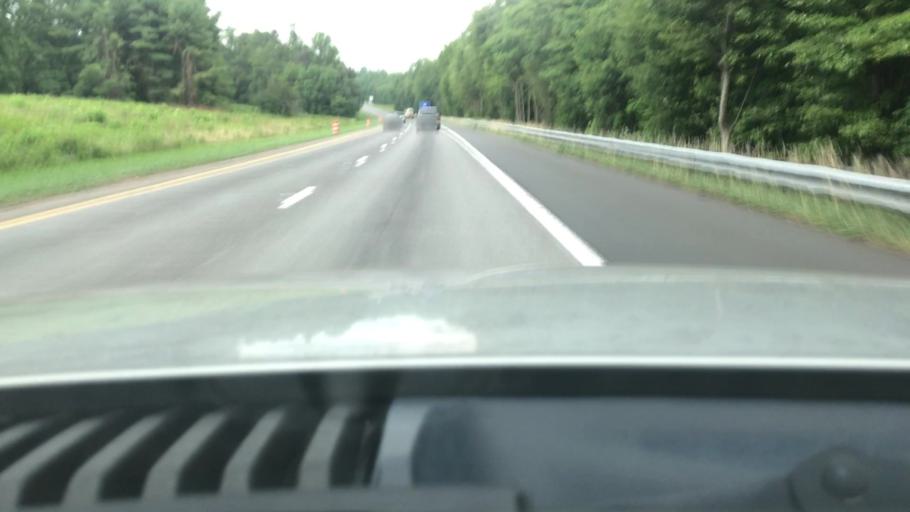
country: US
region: North Carolina
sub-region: Surry County
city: Dobson
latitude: 36.3708
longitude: -80.7935
